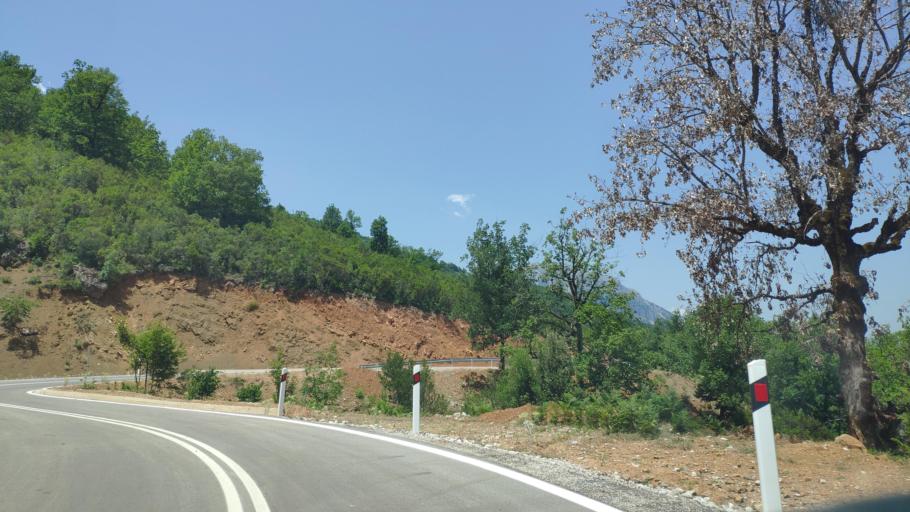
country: GR
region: Epirus
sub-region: Nomos Artas
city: Ano Kalentini
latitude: 39.1855
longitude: 21.3574
